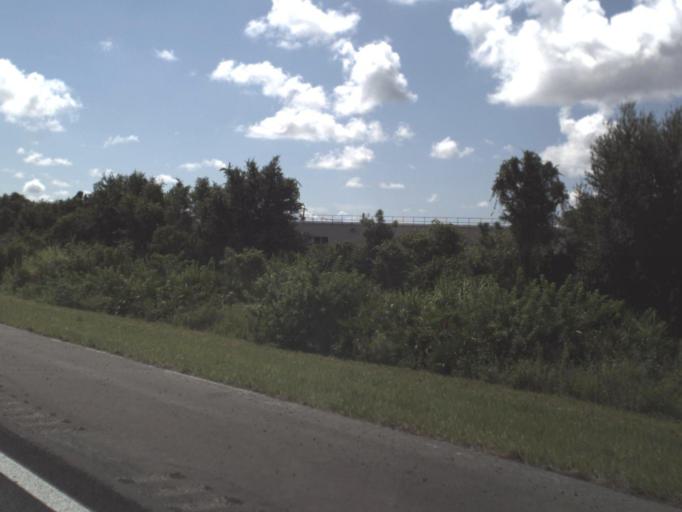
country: US
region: Florida
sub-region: Lee County
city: Suncoast Estates
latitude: 26.7244
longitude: -81.8321
